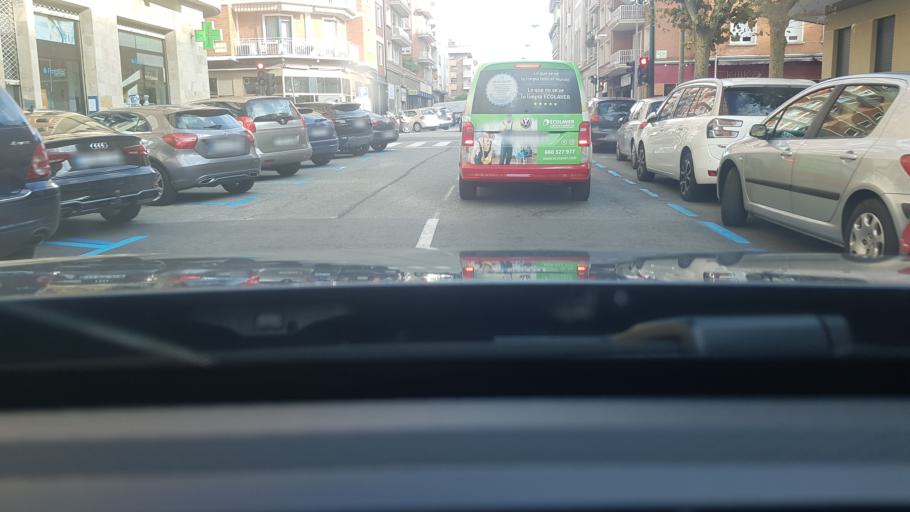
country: ES
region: Navarre
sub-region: Provincia de Navarra
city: Segundo Ensanche
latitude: 42.8093
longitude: -1.6377
